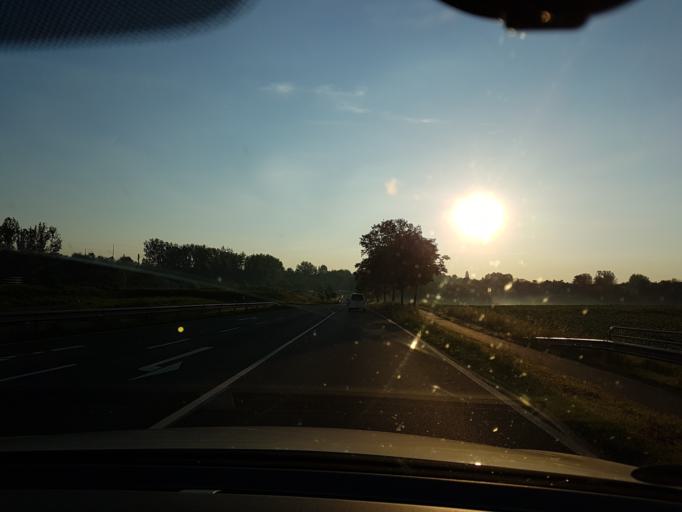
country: DE
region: Lower Saxony
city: Helmstedt
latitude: 52.2134
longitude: 10.9966
